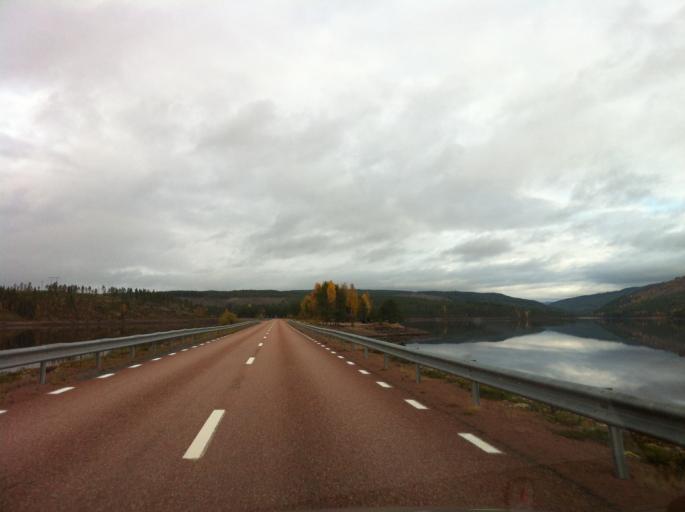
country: SE
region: Dalarna
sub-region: Alvdalens Kommun
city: AElvdalen
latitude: 61.2983
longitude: 13.7297
